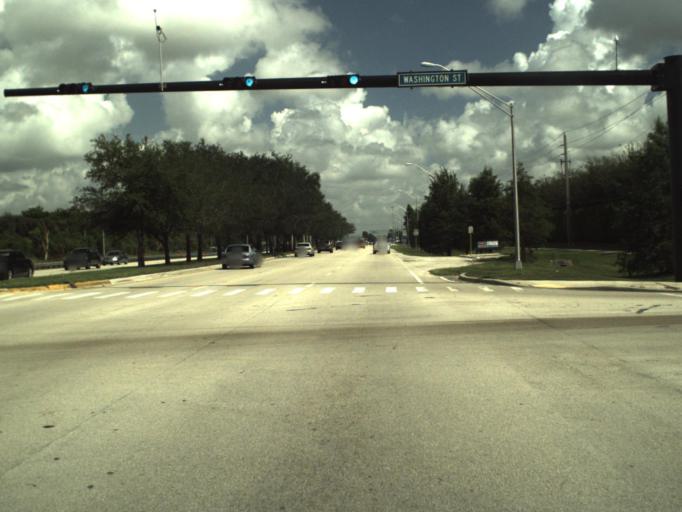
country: US
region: Florida
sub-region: Broward County
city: Sunshine Ranches
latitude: 26.0004
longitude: -80.3116
